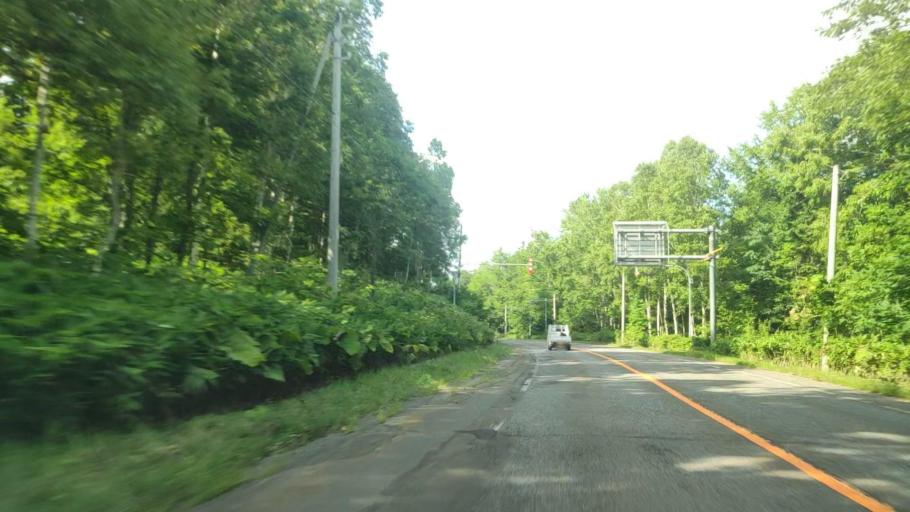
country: JP
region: Hokkaido
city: Nayoro
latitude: 44.3887
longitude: 142.3977
